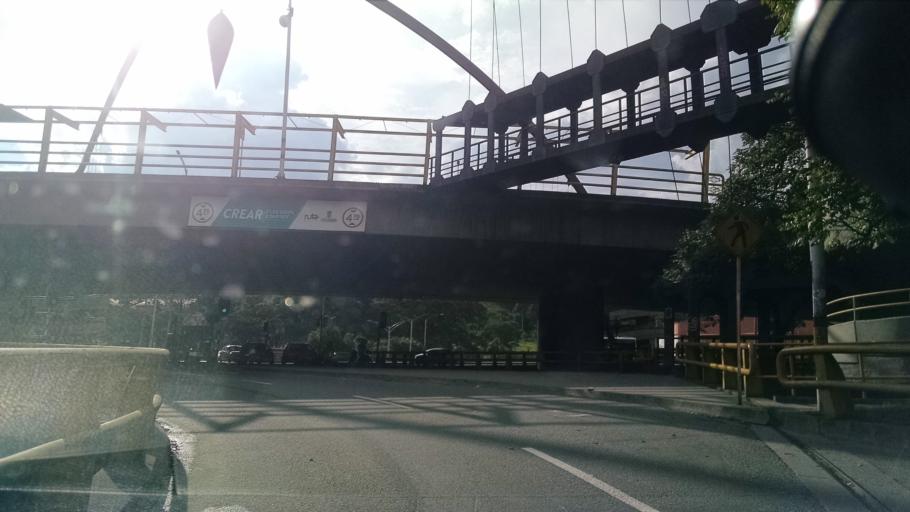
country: CO
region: Antioquia
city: Medellin
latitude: 6.2658
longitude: -75.5745
